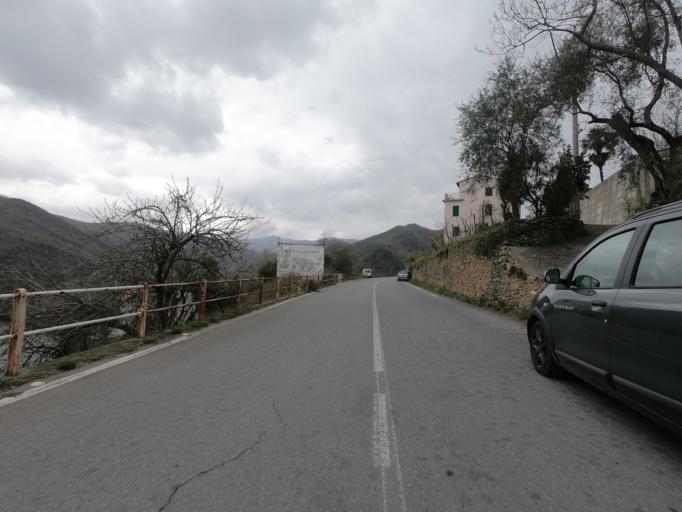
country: IT
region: Liguria
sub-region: Provincia di Savona
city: Casanova Lerrone
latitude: 44.0315
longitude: 8.0470
